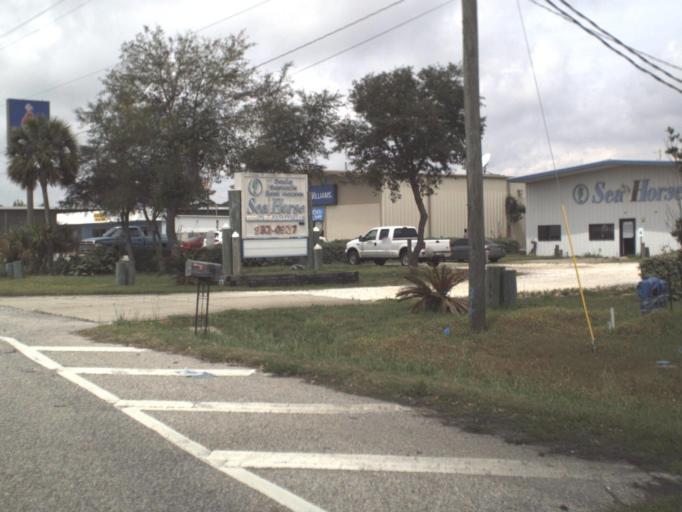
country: US
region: Florida
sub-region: Santa Rosa County
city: Tiger Point
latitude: 30.3930
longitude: -87.0463
